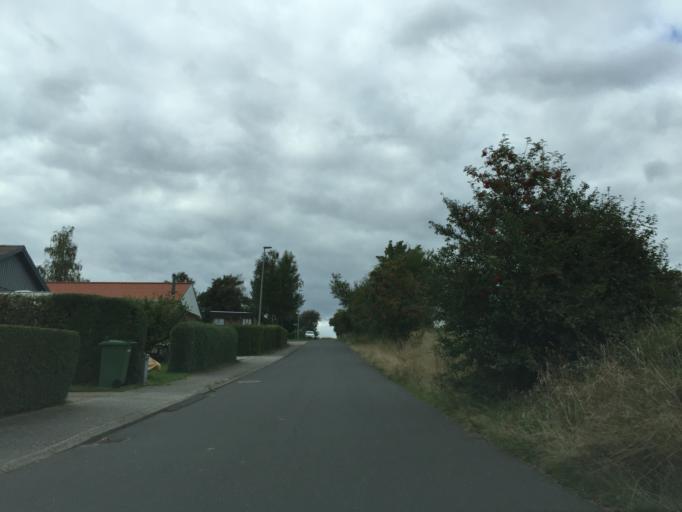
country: DK
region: Central Jutland
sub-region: Silkeborg Kommune
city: Svejbaek
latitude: 56.2310
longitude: 9.7268
